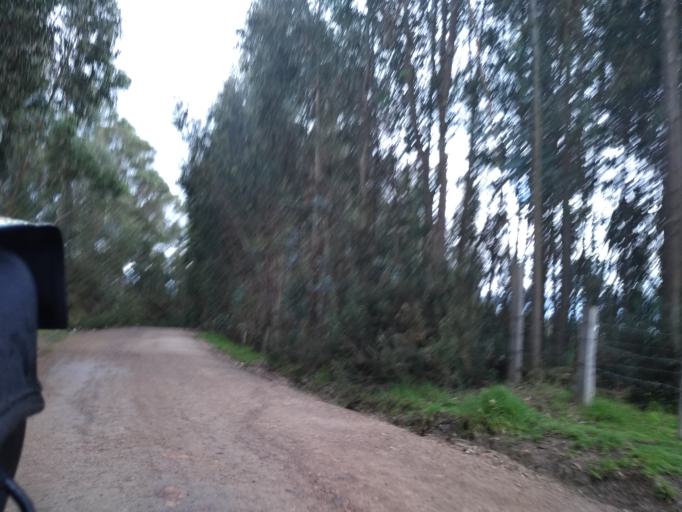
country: CO
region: Boyaca
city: Sotaquira
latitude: 5.7694
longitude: -73.2636
